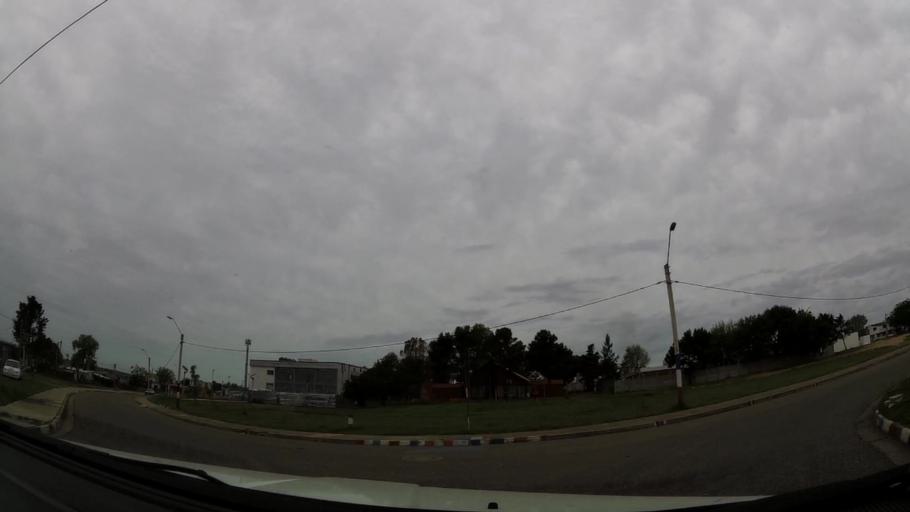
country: UY
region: Maldonado
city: Maldonado
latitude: -34.8938
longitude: -54.9393
